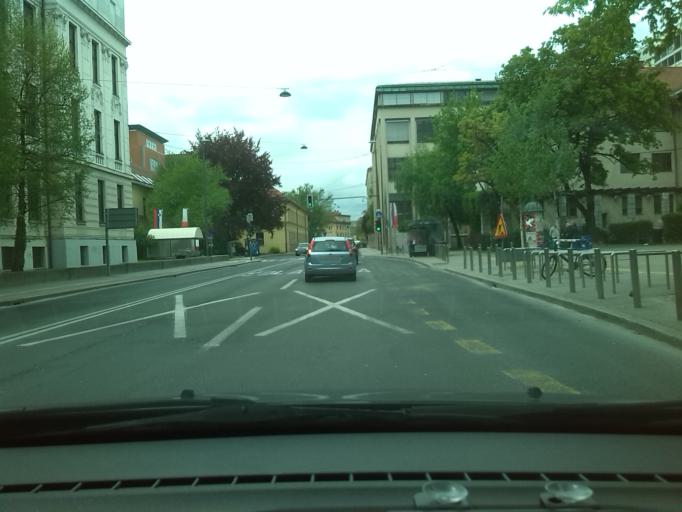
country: SI
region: Ljubljana
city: Ljubljana
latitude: 46.0465
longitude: 14.4999
